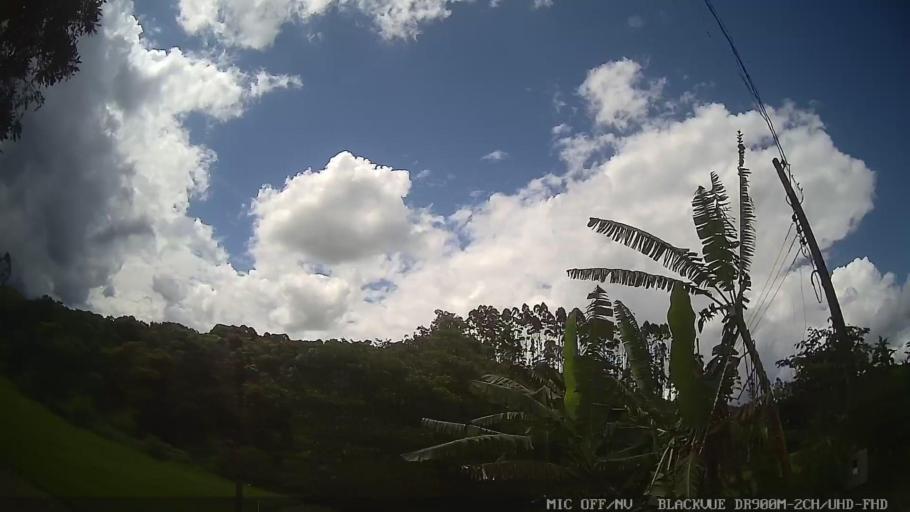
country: BR
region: Sao Paulo
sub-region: Caraguatatuba
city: Caraguatatuba
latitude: -23.5473
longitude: -45.5945
